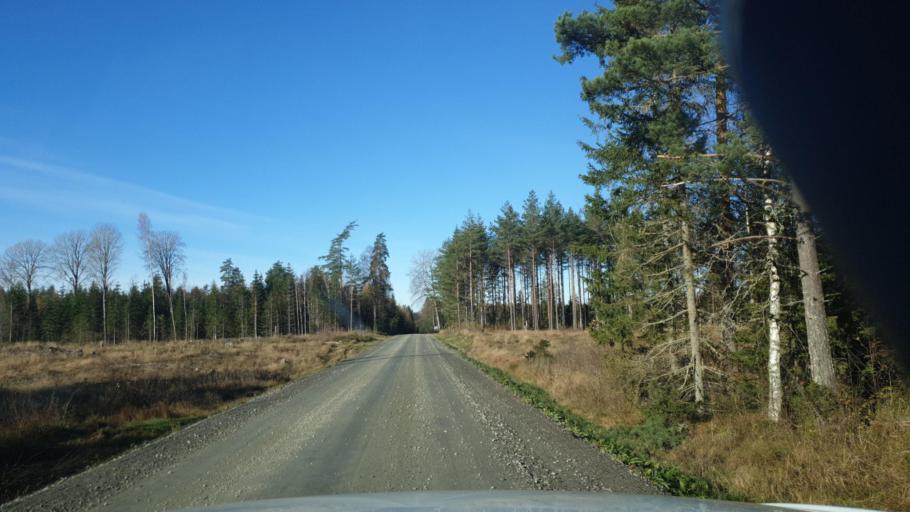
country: SE
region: Vaermland
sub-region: Karlstads Kommun
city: Valberg
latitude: 59.4483
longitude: 13.1113
